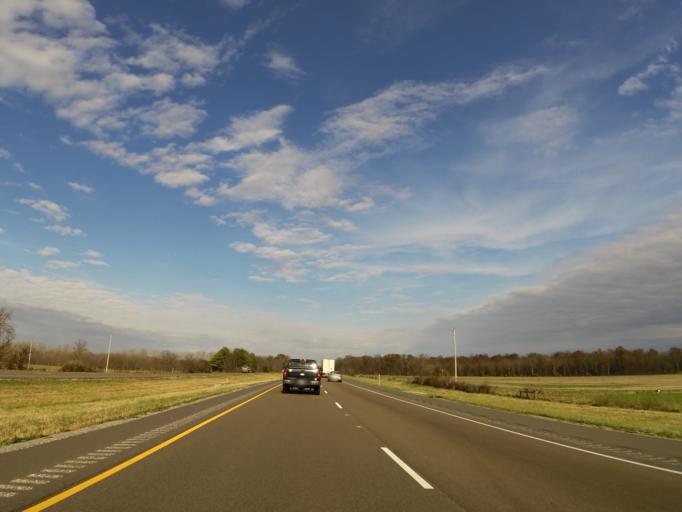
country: US
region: Illinois
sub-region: Washington County
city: Okawville
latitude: 38.4620
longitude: -89.5684
